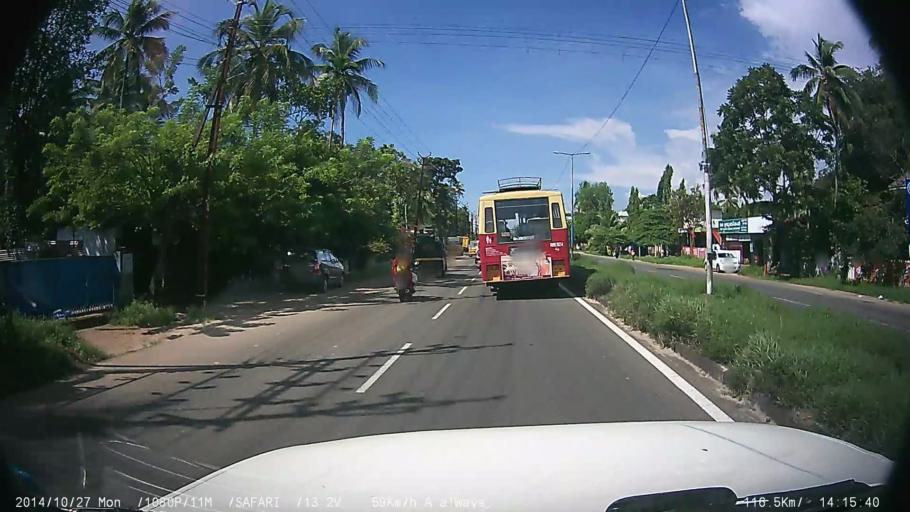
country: IN
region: Kerala
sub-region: Alappuzha
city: Kutiatodu
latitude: 9.8348
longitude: 76.3094
